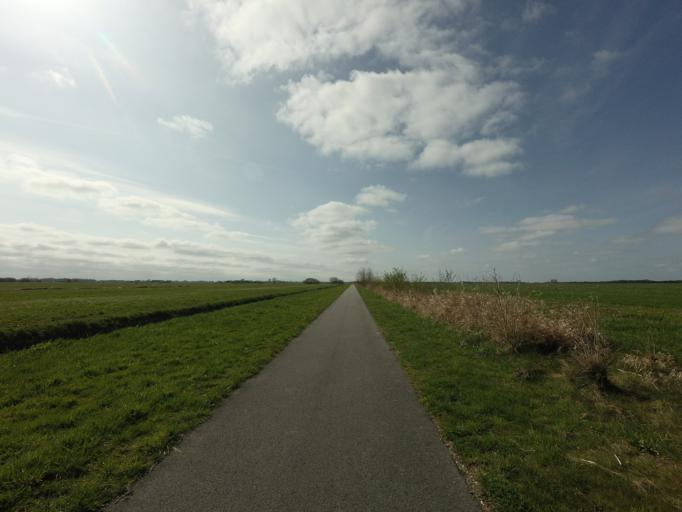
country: NL
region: North Holland
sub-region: Gemeente Wijdemeren
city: Nieuw-Loosdrecht
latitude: 52.1757
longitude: 5.1509
